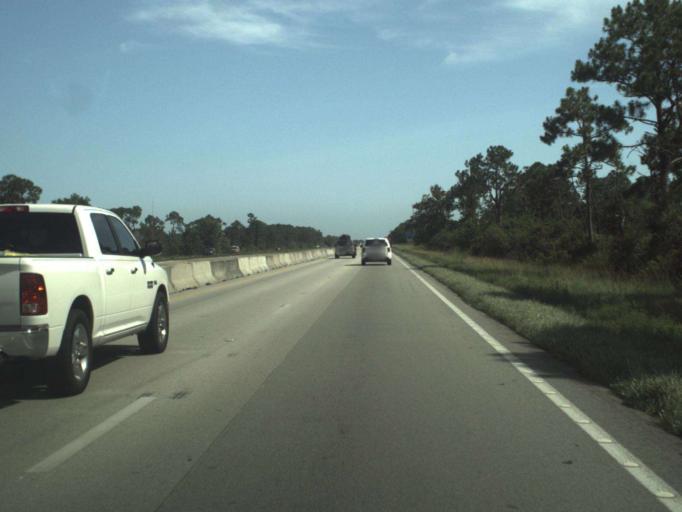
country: US
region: Florida
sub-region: Indian River County
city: Fellsmere
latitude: 27.7096
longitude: -80.5421
